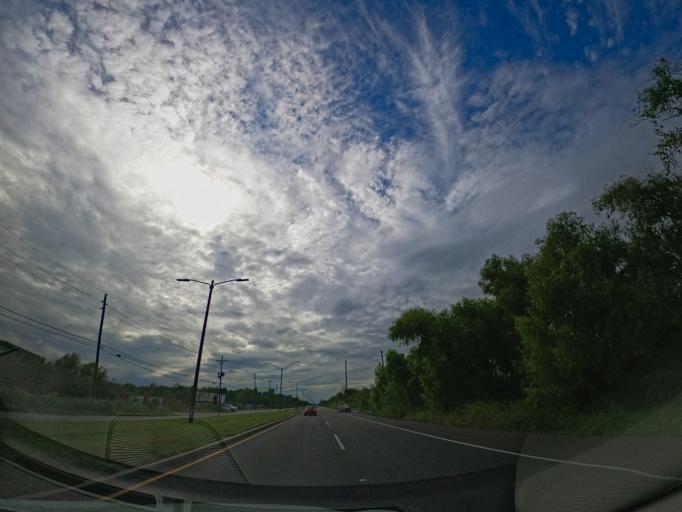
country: US
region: Louisiana
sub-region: Saint Bernard Parish
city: Chalmette
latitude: 30.0103
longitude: -89.9664
